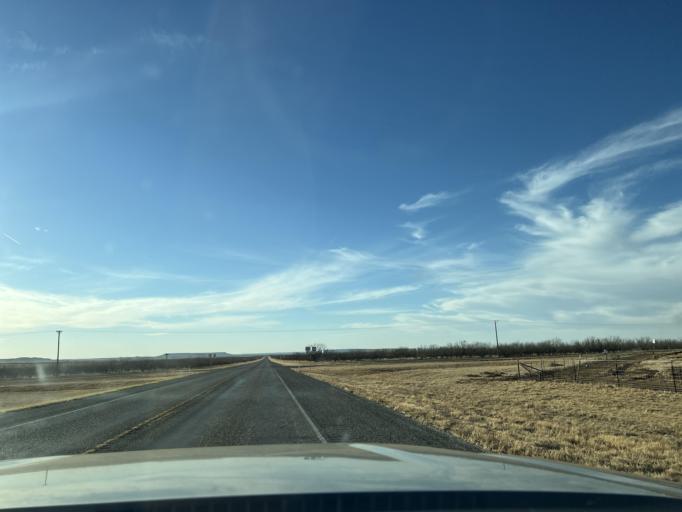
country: US
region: Texas
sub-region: Borden County
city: Gail
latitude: 32.7661
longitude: -101.2889
